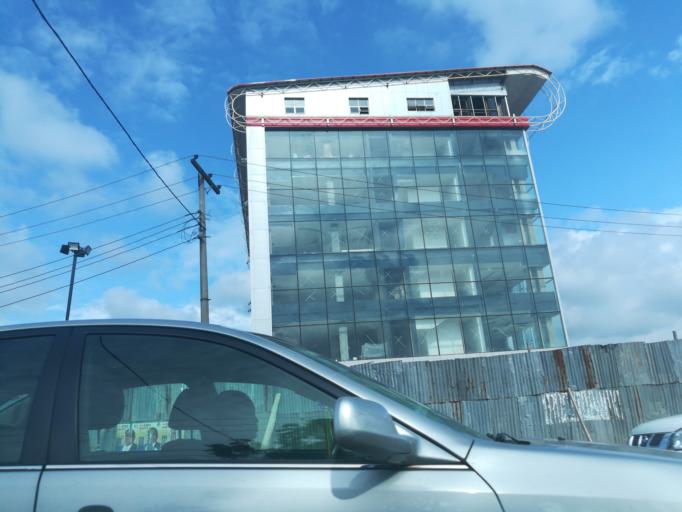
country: NG
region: Lagos
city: Agege
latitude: 6.6237
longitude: 3.3525
